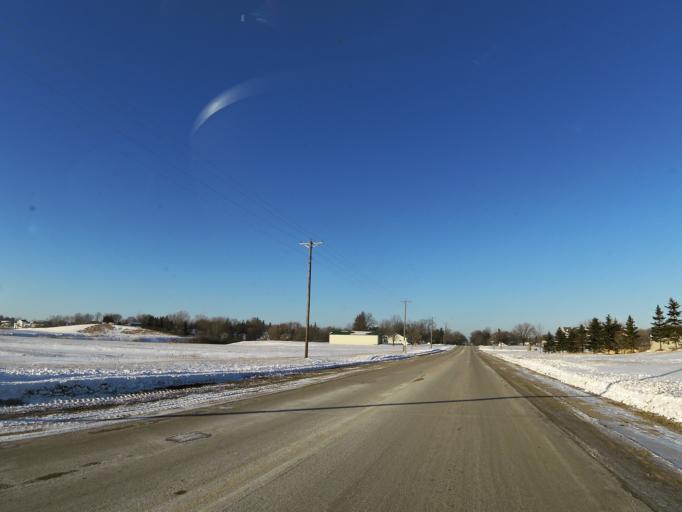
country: US
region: Minnesota
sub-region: Rice County
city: Lonsdale
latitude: 44.4720
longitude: -93.4285
